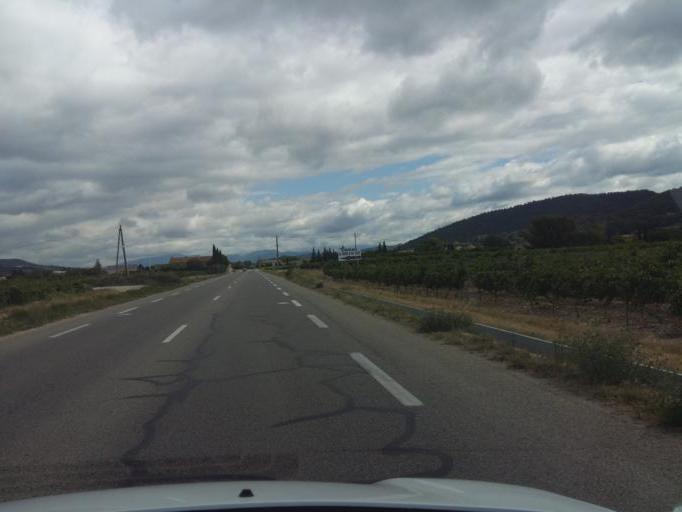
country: FR
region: Provence-Alpes-Cote d'Azur
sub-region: Departement du Vaucluse
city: Sablet
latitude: 44.2146
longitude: 5.0053
